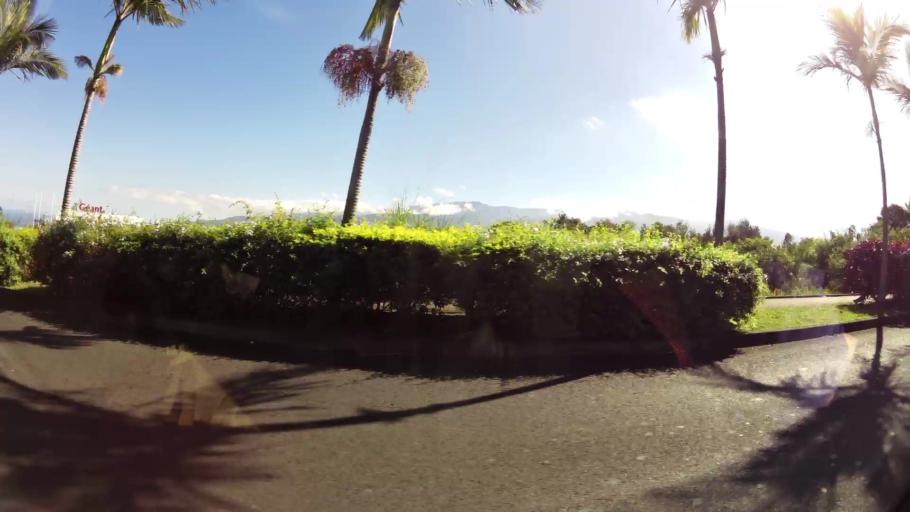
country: RE
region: Reunion
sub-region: Reunion
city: Le Tampon
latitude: -21.2734
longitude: 55.5093
